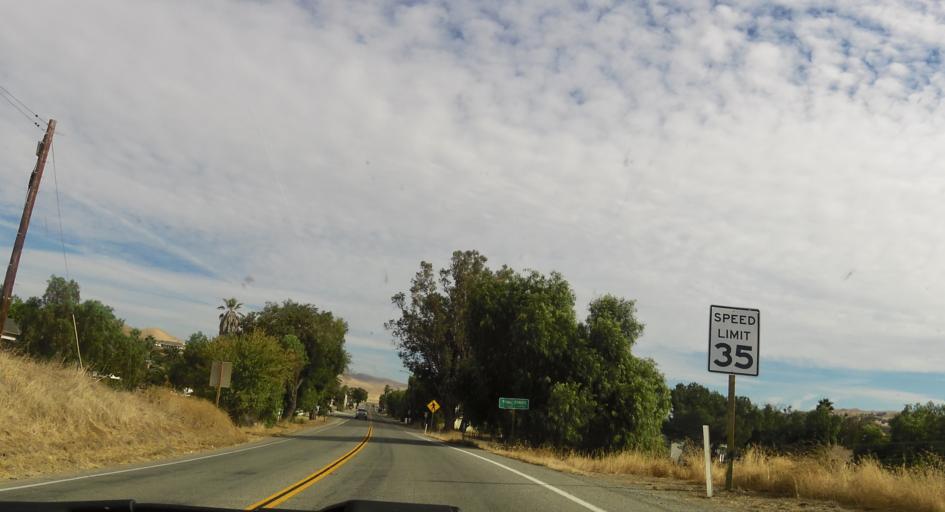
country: US
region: California
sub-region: San Benito County
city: Ridgemark
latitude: 36.7911
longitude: -121.3236
